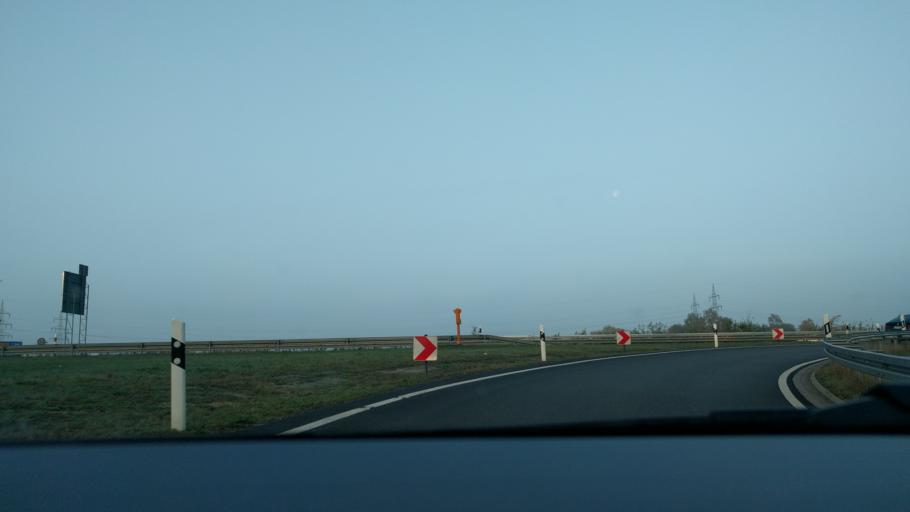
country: DE
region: Lower Saxony
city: Weyhausen
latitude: 52.4340
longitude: 10.7380
